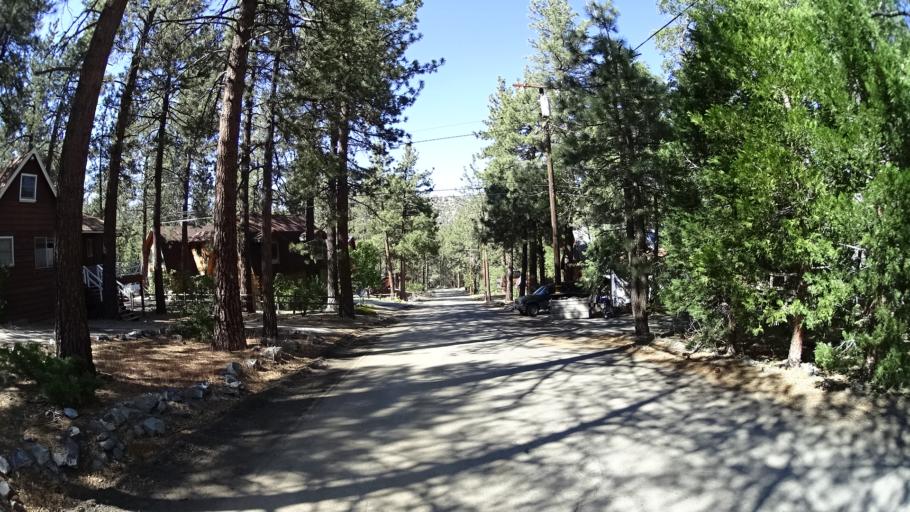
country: US
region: California
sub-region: San Bernardino County
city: Wrightwood
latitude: 34.3558
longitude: -117.6399
